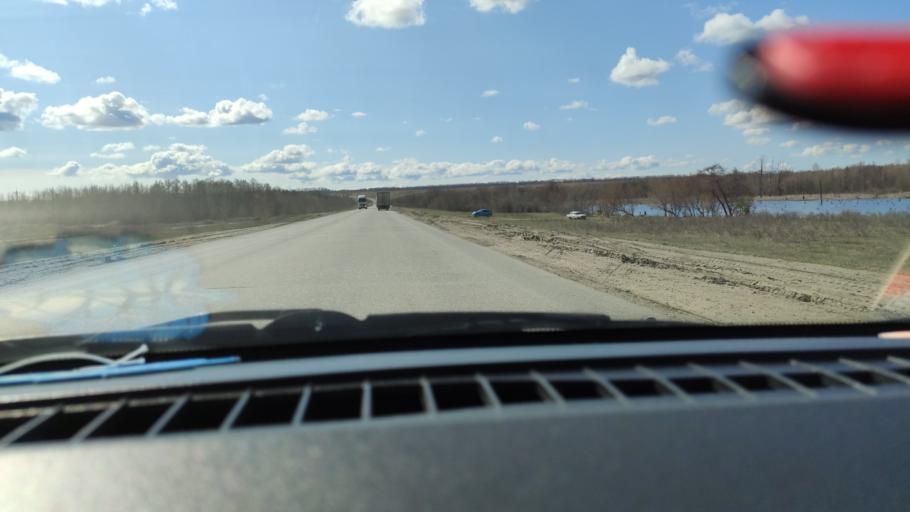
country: RU
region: Samara
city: Varlamovo
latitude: 53.1357
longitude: 48.2867
